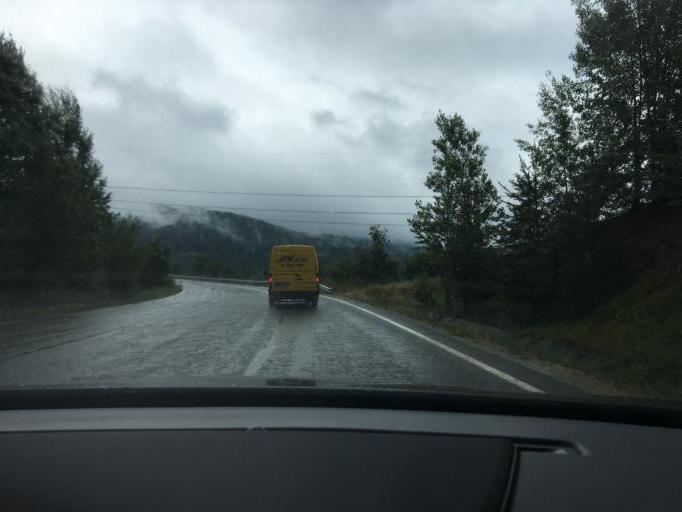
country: BG
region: Kyustendil
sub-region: Obshtina Kyustendil
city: Kyustendil
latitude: 42.2646
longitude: 22.5837
